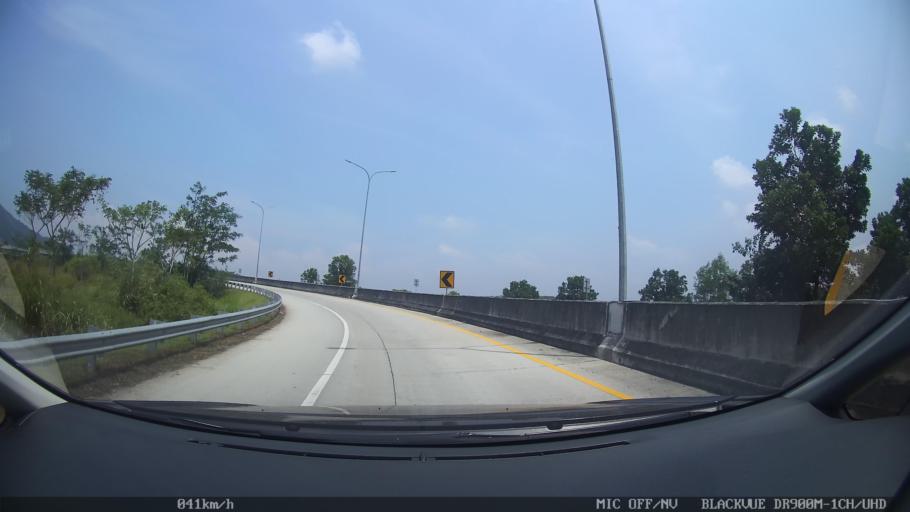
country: ID
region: Lampung
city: Panjang
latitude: -5.3959
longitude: 105.3510
